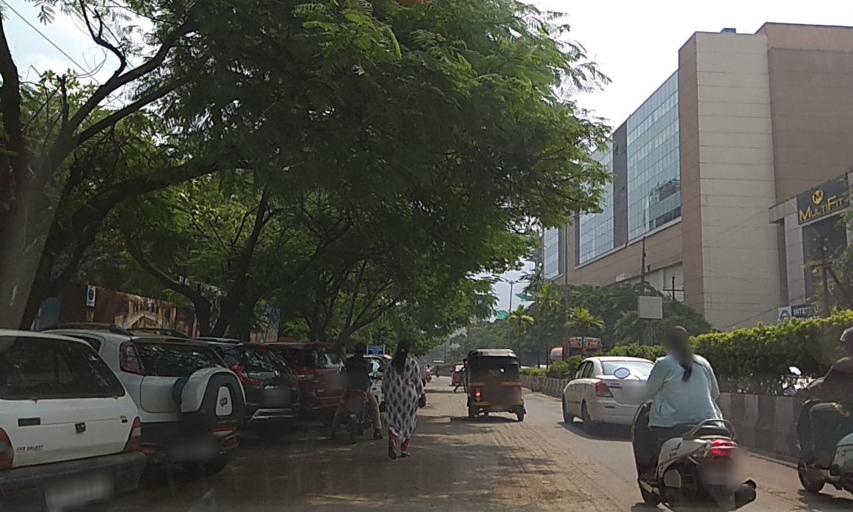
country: IN
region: Maharashtra
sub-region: Pune Division
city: Lohogaon
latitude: 18.5640
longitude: 73.9181
